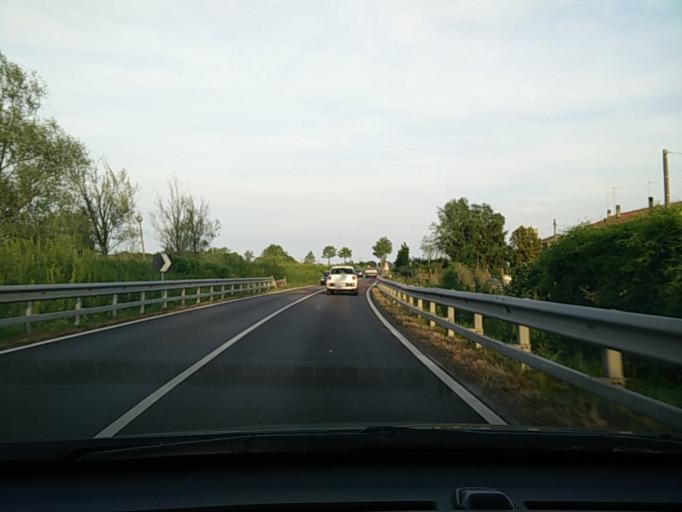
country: IT
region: Veneto
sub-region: Provincia di Venezia
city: Quarto d'Altino
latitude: 45.5625
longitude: 12.4207
